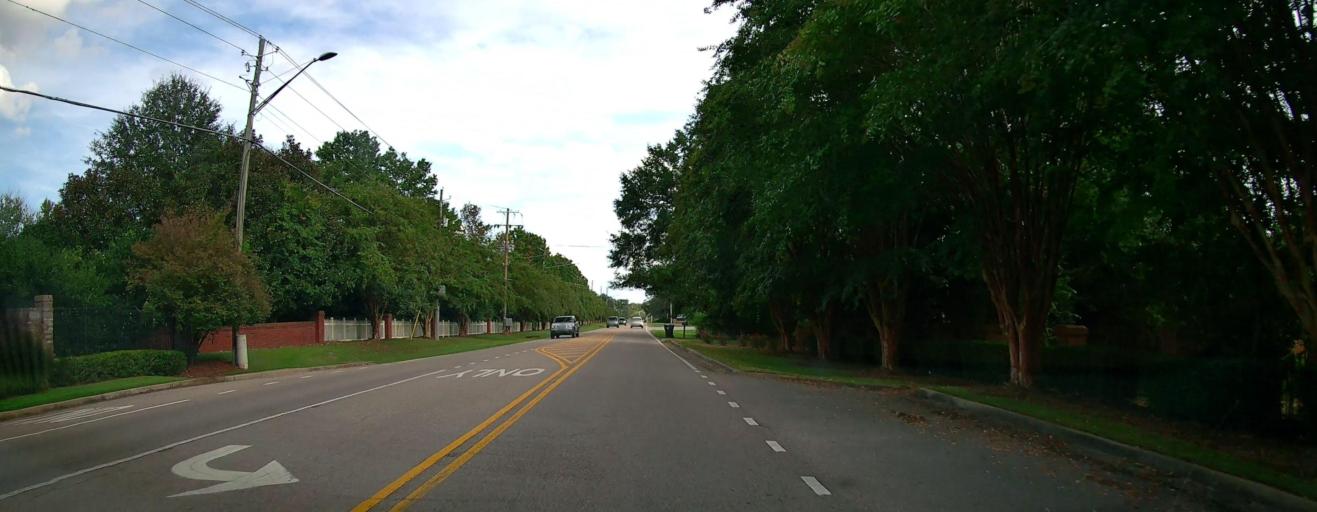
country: US
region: Alabama
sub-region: Russell County
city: Phenix City
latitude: 32.5157
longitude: -85.0248
